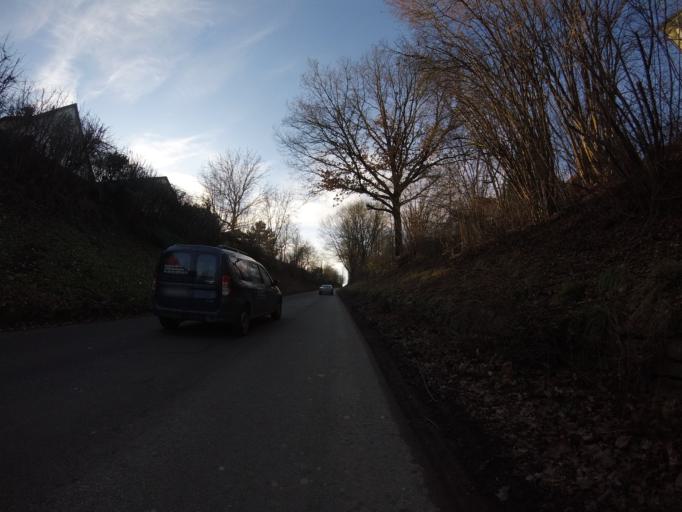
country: DE
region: Baden-Wuerttemberg
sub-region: Regierungsbezirk Stuttgart
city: Allmersbach im Tal
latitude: 48.9306
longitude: 9.4714
